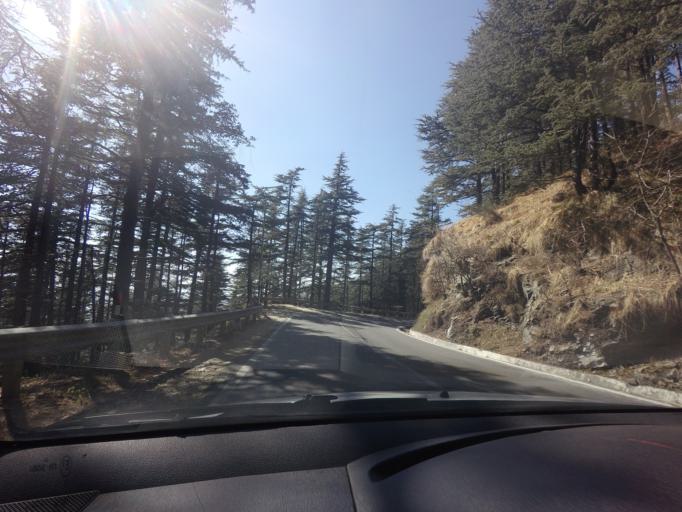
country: IN
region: Himachal Pradesh
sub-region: Shimla
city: Shimla
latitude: 31.1133
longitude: 77.2221
